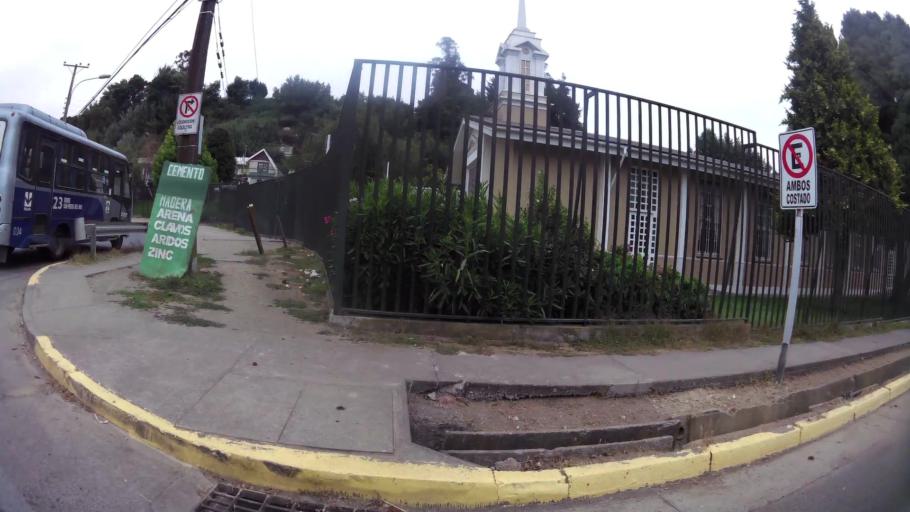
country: CL
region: Biobio
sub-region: Provincia de Concepcion
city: Concepcion
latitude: -36.8347
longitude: -73.0054
